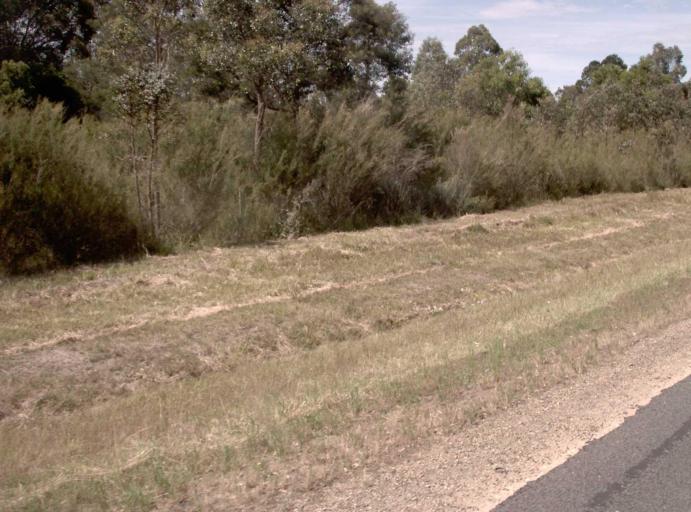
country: AU
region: Victoria
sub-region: East Gippsland
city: Bairnsdale
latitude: -37.9043
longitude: 147.3391
